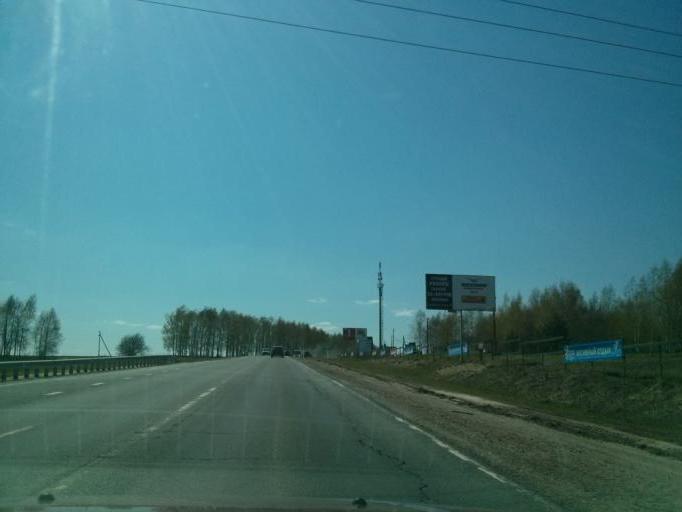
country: RU
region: Nizjnij Novgorod
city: Burevestnik
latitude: 56.1965
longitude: 43.8456
